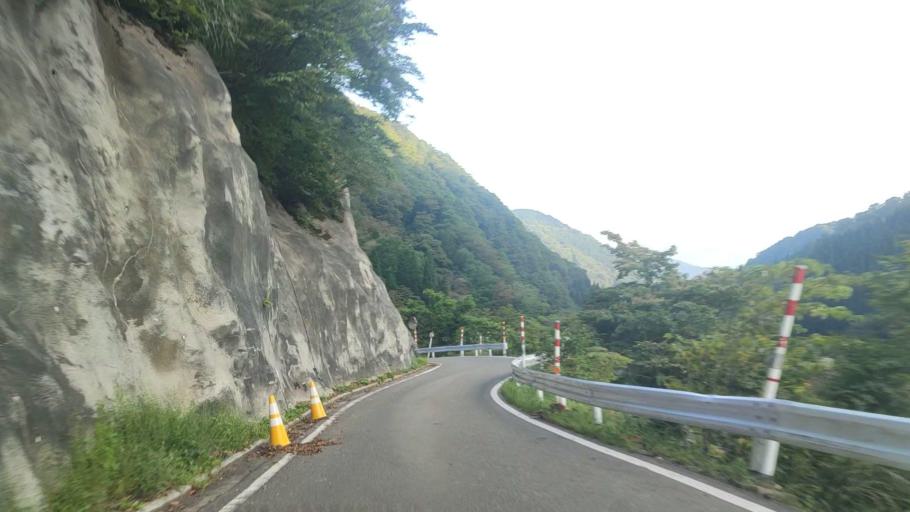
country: JP
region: Toyama
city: Yatsuomachi-higashikumisaka
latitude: 36.4984
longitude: 137.0492
